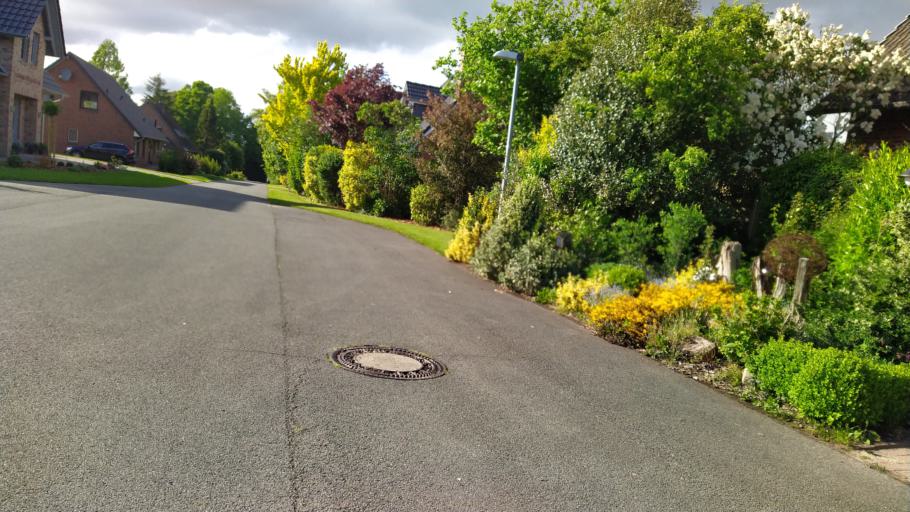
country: DE
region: Lower Saxony
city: Farven
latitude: 53.4347
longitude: 9.3270
